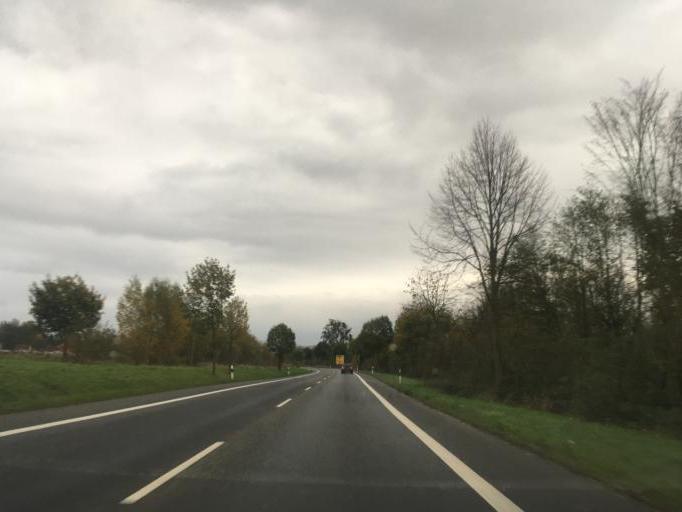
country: DE
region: Lower Saxony
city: Hardegsen
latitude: 51.6439
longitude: 9.8637
